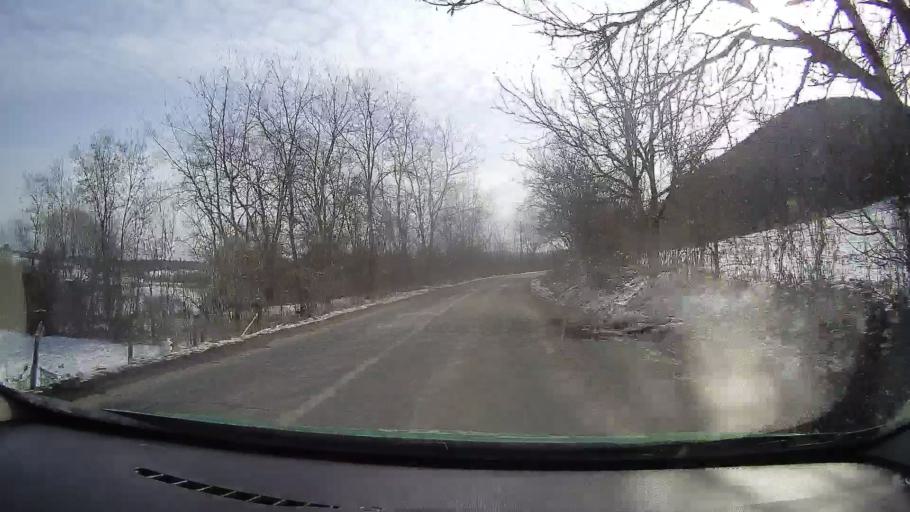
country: RO
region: Mures
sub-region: Comuna Apold
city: Saes
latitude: 46.1924
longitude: 24.7649
